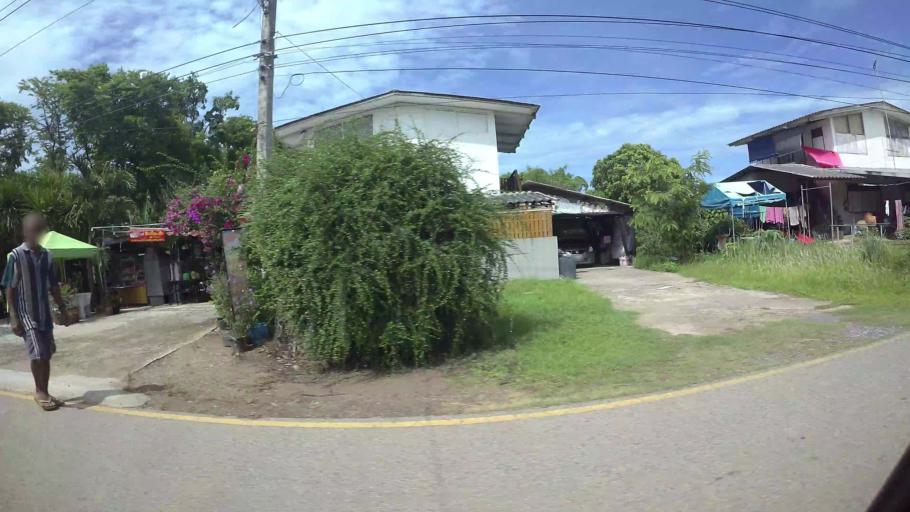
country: TH
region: Chon Buri
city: Sattahip
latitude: 12.6641
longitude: 100.9155
